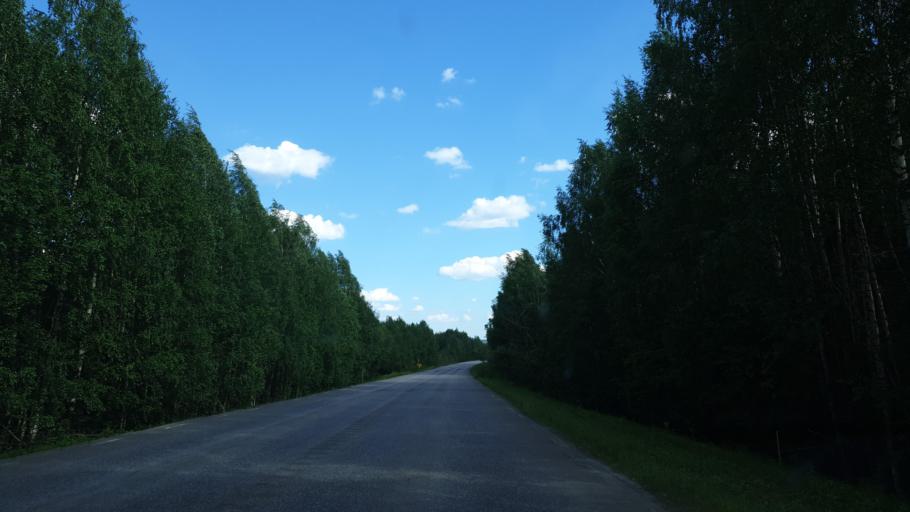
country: SE
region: Norrbotten
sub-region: Alvsbyns Kommun
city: AElvsbyn
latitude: 65.8431
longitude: 20.4953
